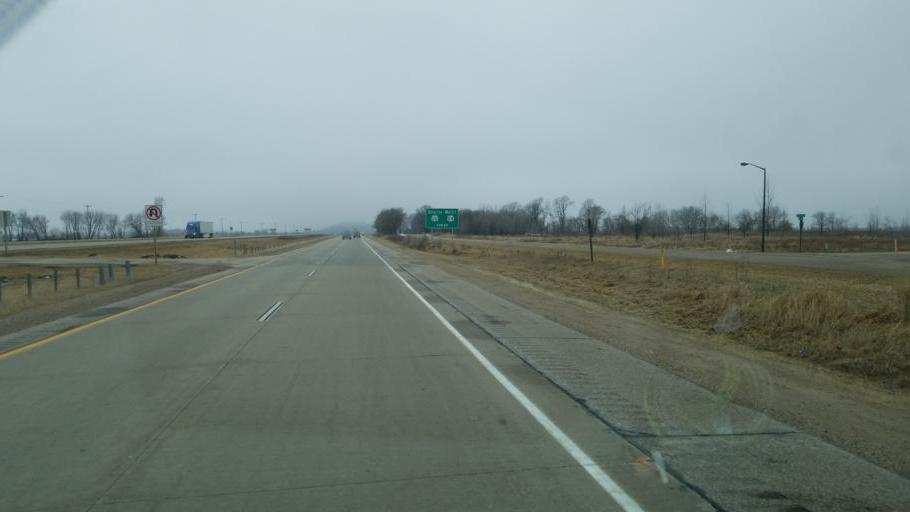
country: US
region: Wisconsin
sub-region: Waupaca County
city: Waupaca
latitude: 44.3295
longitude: -89.0225
